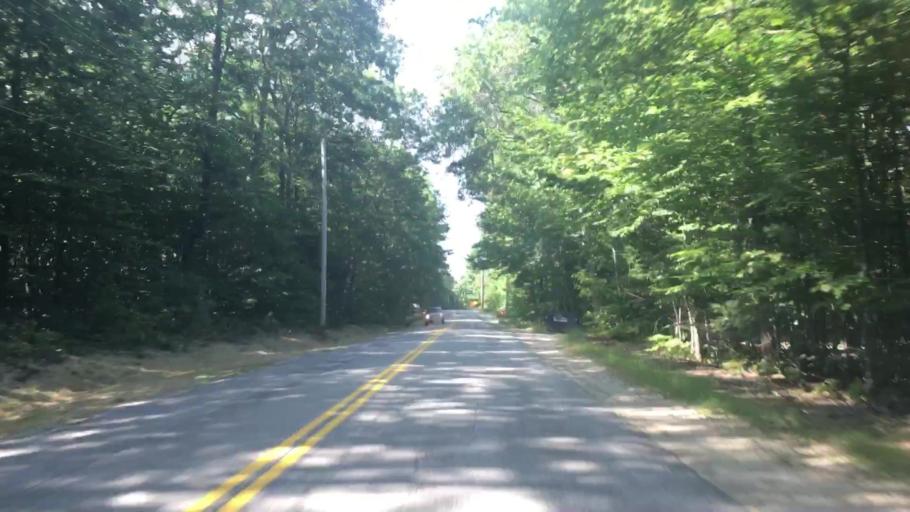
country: US
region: Maine
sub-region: Androscoggin County
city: Poland
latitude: 44.0217
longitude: -70.4251
